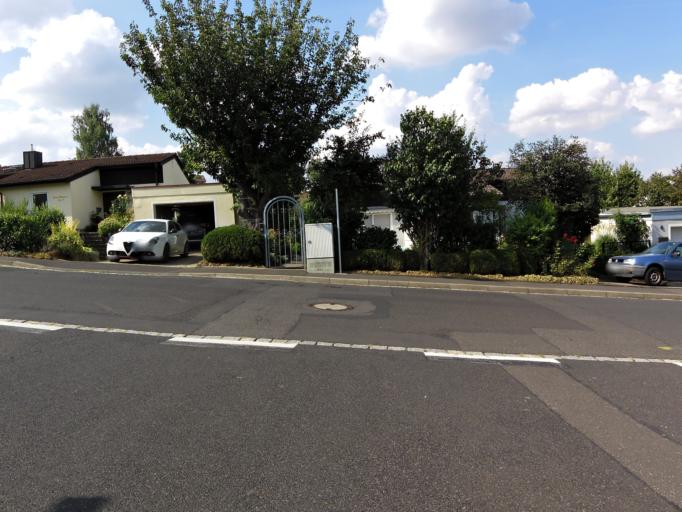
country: DE
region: Bavaria
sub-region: Regierungsbezirk Unterfranken
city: Estenfeld
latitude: 49.8236
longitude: 10.0034
